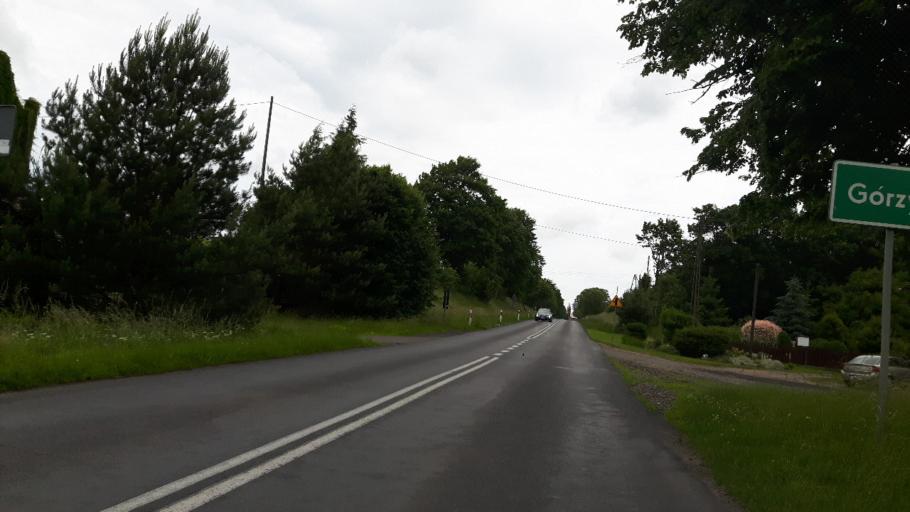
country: PL
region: West Pomeranian Voivodeship
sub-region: Powiat gryficki
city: Gryfice
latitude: 53.9693
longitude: 15.2323
